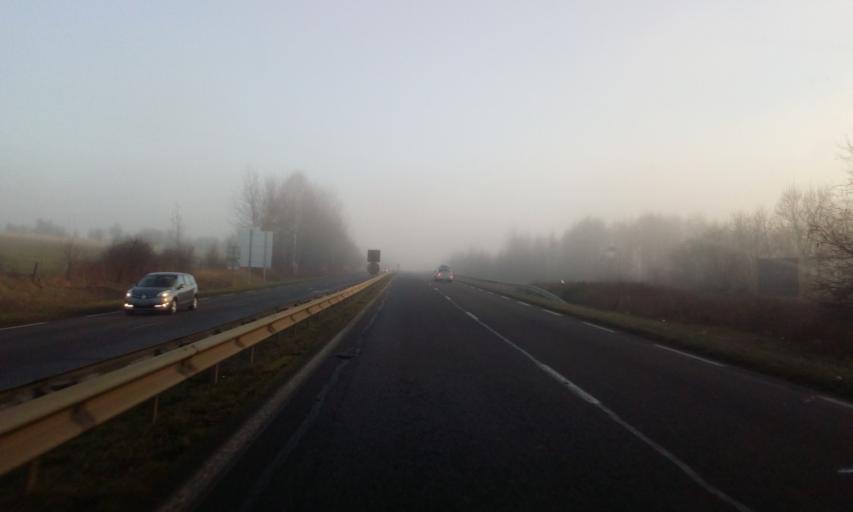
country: FR
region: Champagne-Ardenne
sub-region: Departement des Ardennes
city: Tournes
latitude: 49.8020
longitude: 4.6252
